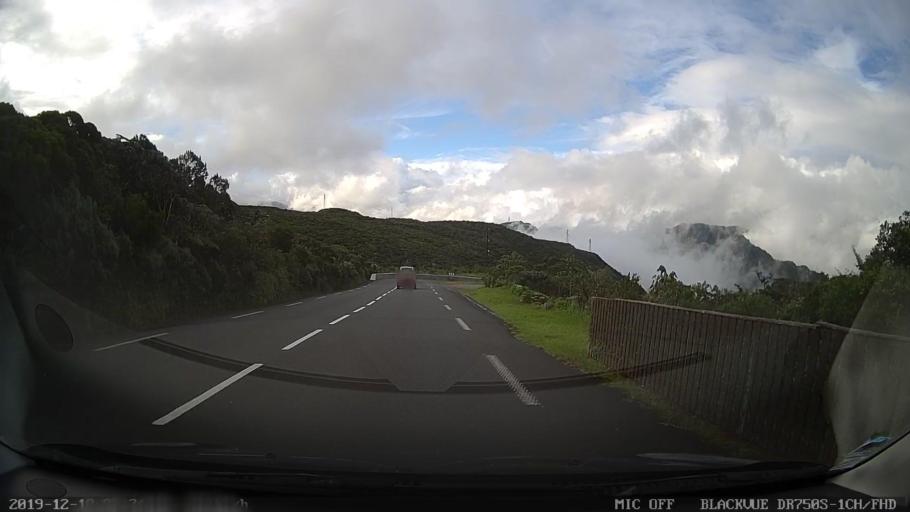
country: RE
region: Reunion
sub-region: Reunion
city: Cilaos
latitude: -21.1636
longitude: 55.5909
